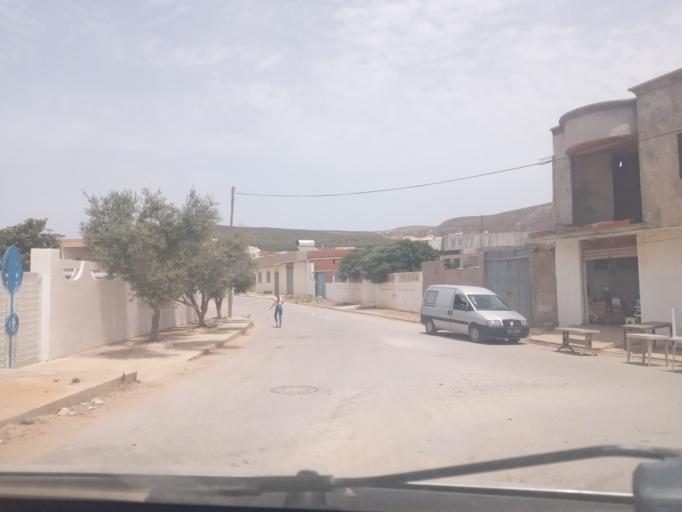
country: TN
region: Nabul
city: El Haouaria
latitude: 37.0536
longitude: 11.0095
